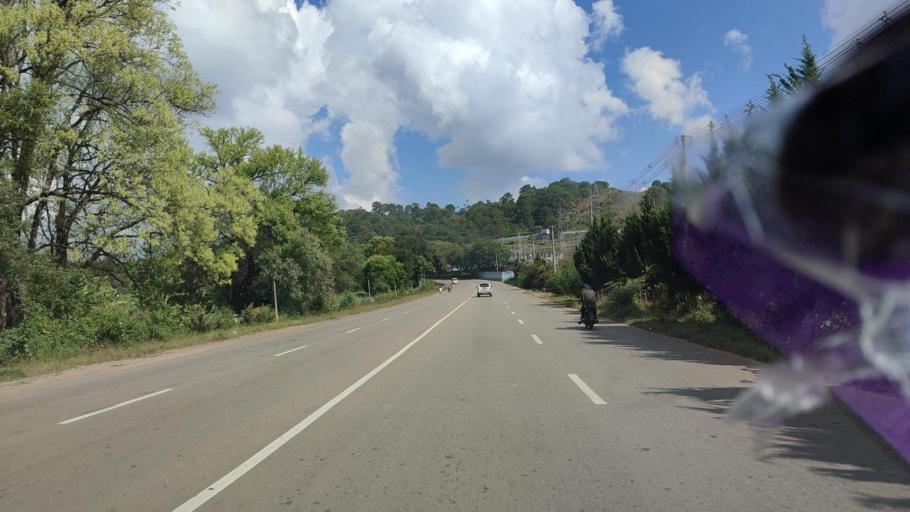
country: MM
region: Shan
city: Taunggyi
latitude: 20.6412
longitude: 96.5901
